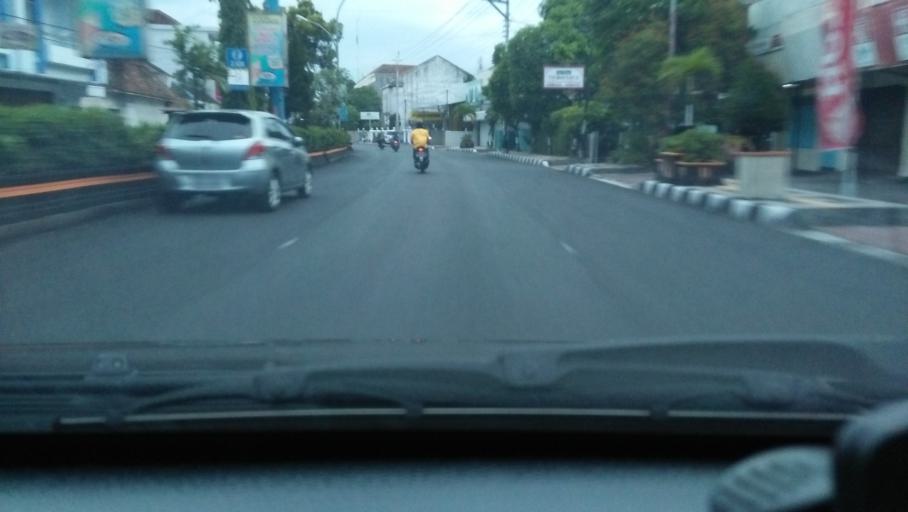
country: ID
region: Central Java
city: Magelang
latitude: -7.4714
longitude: 110.2177
